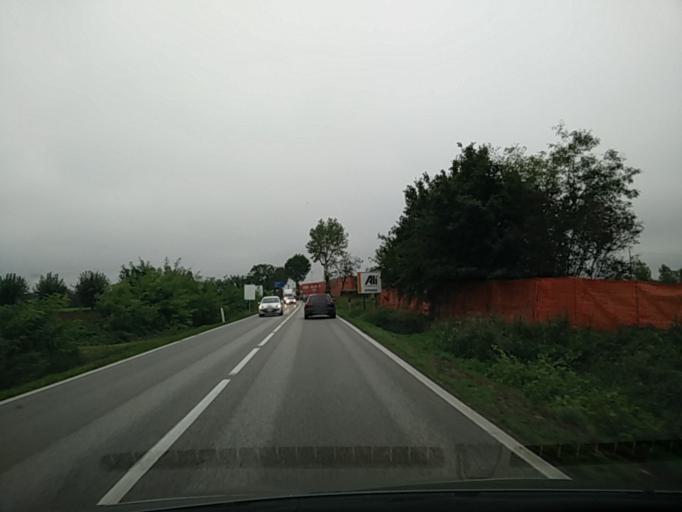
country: IT
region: Veneto
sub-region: Provincia di Treviso
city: Ospedaletto
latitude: 45.6798
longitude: 12.0816
